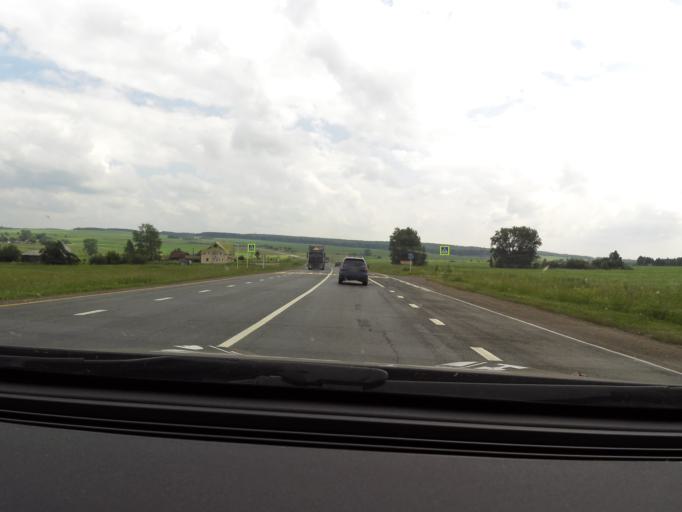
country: RU
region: Sverdlovsk
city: Achit
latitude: 56.8946
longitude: 57.6042
